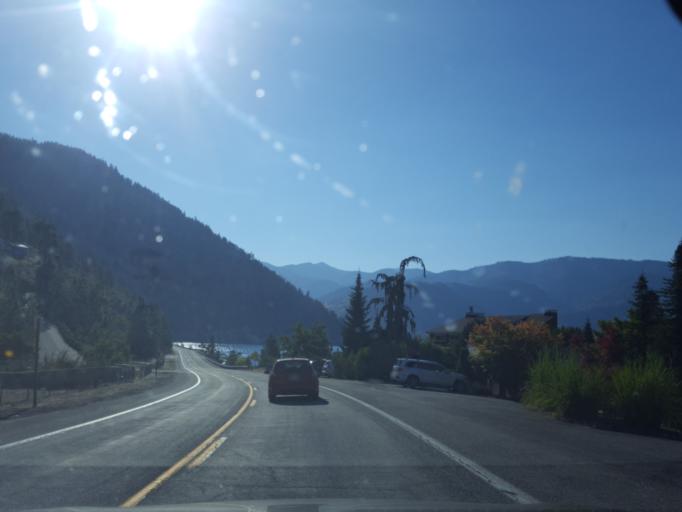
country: US
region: Washington
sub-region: Chelan County
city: Manson
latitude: 47.8601
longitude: -120.1510
